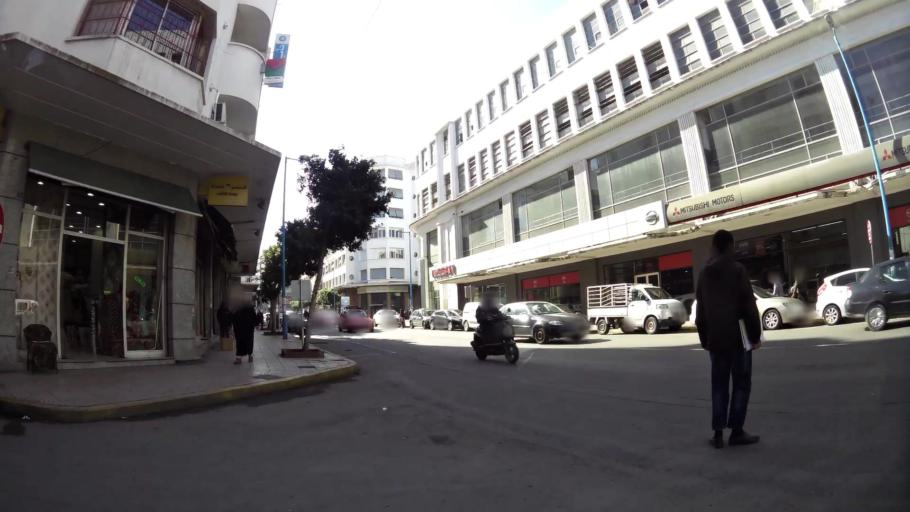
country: MA
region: Grand Casablanca
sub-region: Casablanca
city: Casablanca
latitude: 33.5904
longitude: -7.6120
